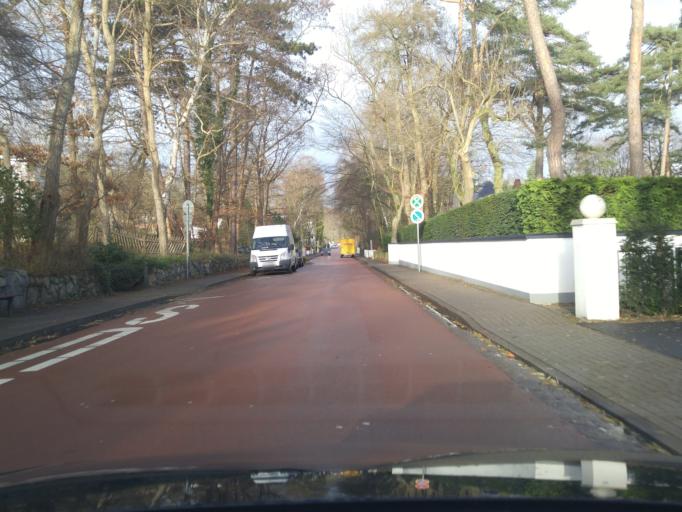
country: DE
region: Schleswig-Holstein
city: Timmendorfer Strand
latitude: 54.0055
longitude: 10.7744
